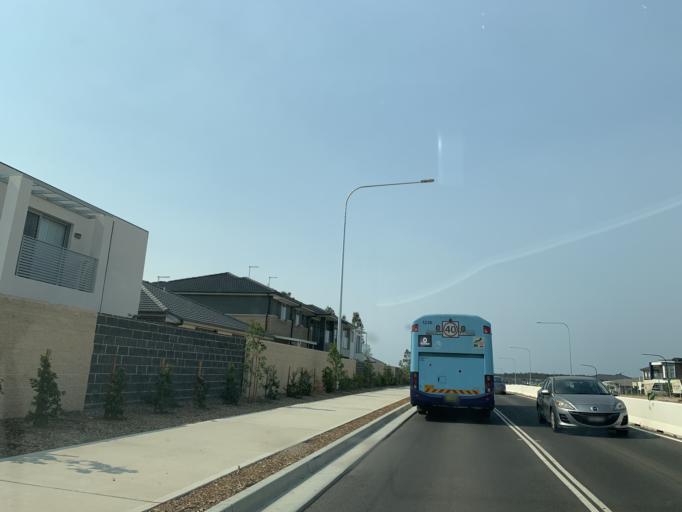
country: AU
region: New South Wales
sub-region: Blacktown
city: Quakers Hill
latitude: -33.7075
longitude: 150.8938
